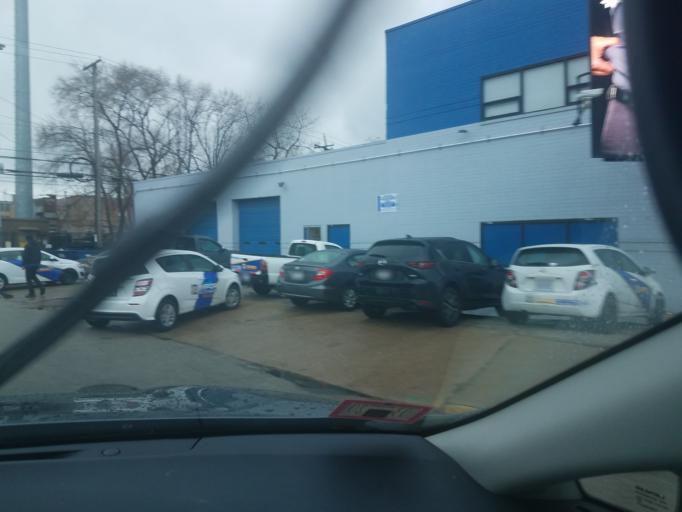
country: US
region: Illinois
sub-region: Cook County
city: Chicago
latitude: 41.8908
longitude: -87.6745
